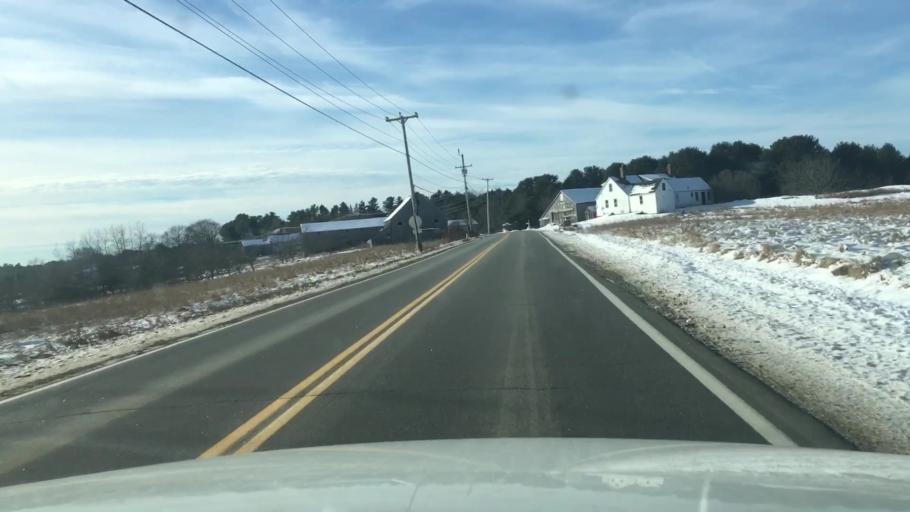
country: US
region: Maine
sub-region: Lincoln County
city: Wiscasset
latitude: 43.9694
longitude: -69.6953
